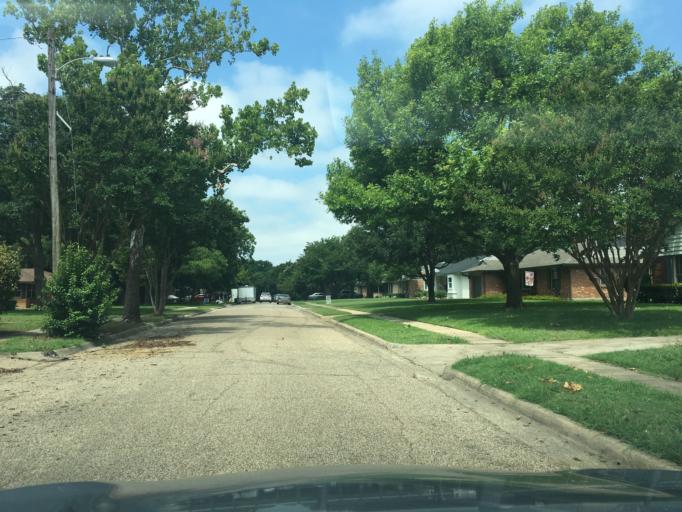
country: US
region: Texas
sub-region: Dallas County
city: Richardson
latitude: 32.9453
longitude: -96.7455
